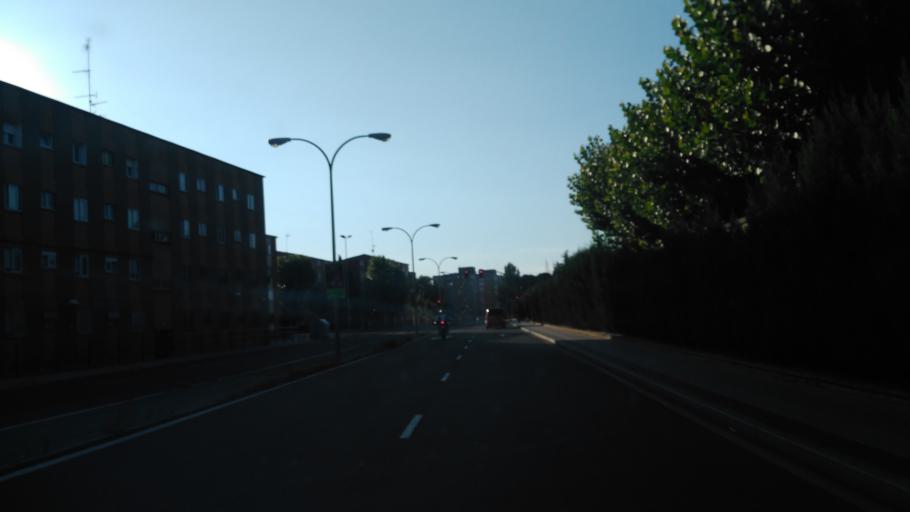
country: ES
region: Castille and Leon
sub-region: Provincia de Salamanca
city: Carbajosa de la Sagrada
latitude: 40.9489
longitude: -5.6577
